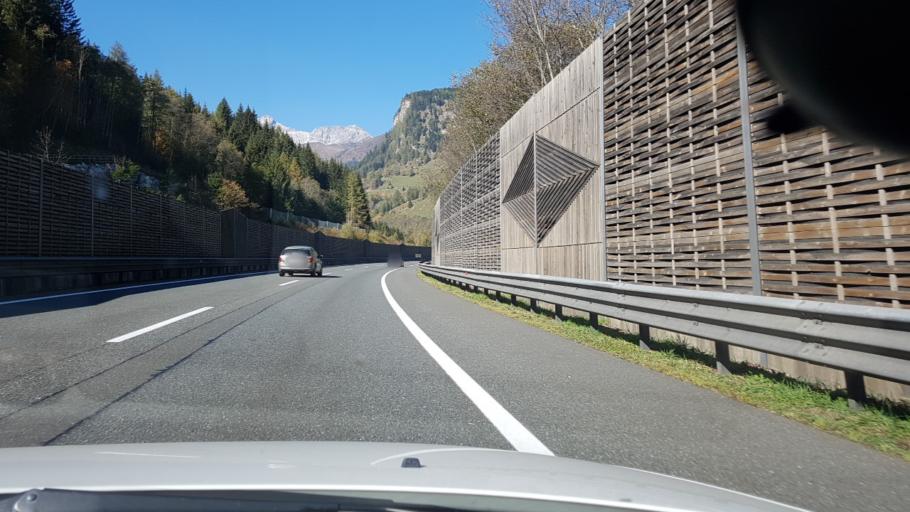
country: AT
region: Salzburg
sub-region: Politischer Bezirk Tamsweg
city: Zederhaus
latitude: 47.1651
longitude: 13.4676
